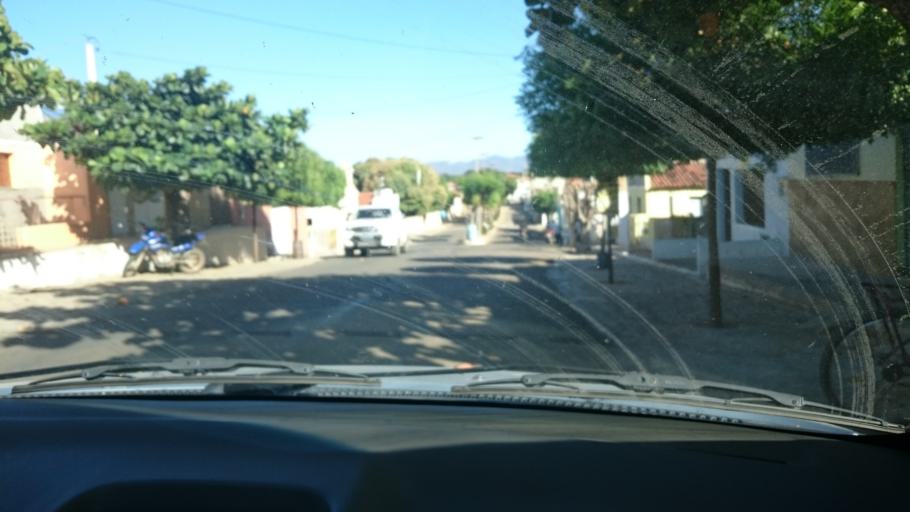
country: BR
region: Paraiba
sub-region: Catole Do Rocha
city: Sao Bento
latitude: -6.1544
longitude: -37.7633
